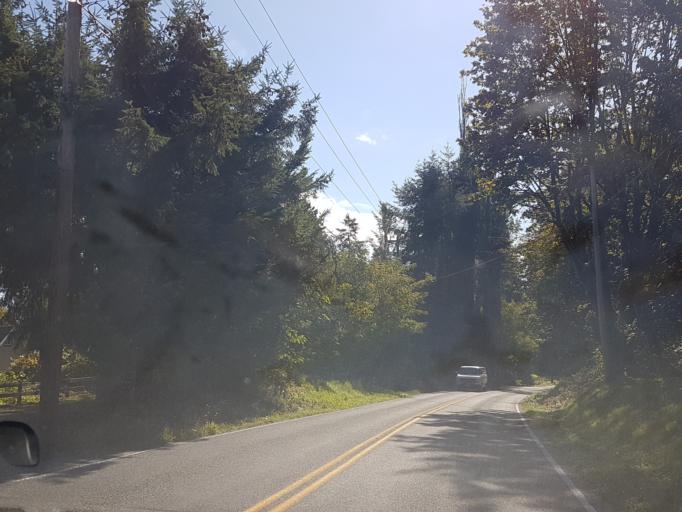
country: US
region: Washington
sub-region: Snohomish County
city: Cathcart
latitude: 47.8465
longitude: -122.0984
